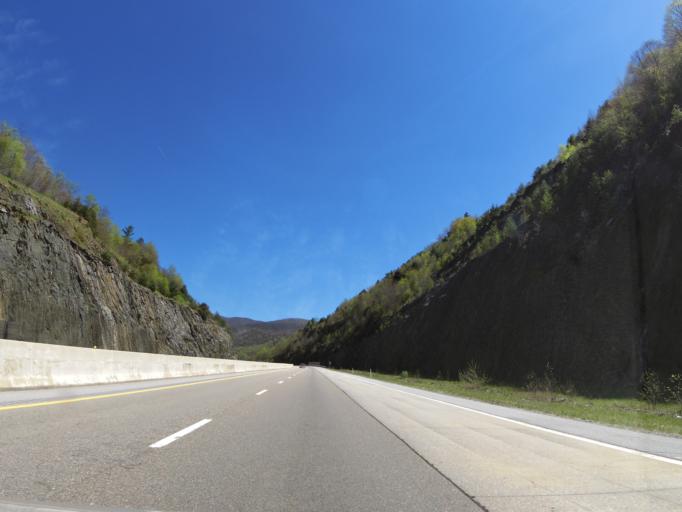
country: US
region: Tennessee
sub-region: Unicoi County
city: Banner Hill
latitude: 36.0084
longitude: -82.5445
